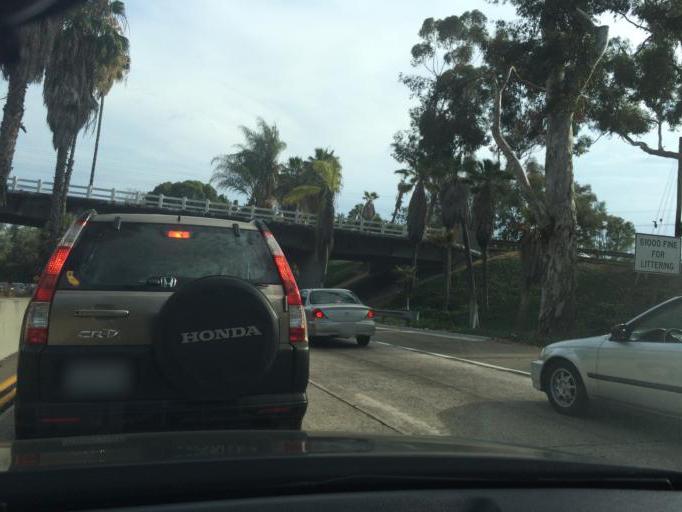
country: US
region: California
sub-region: San Diego County
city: San Diego
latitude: 32.7472
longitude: -117.1564
